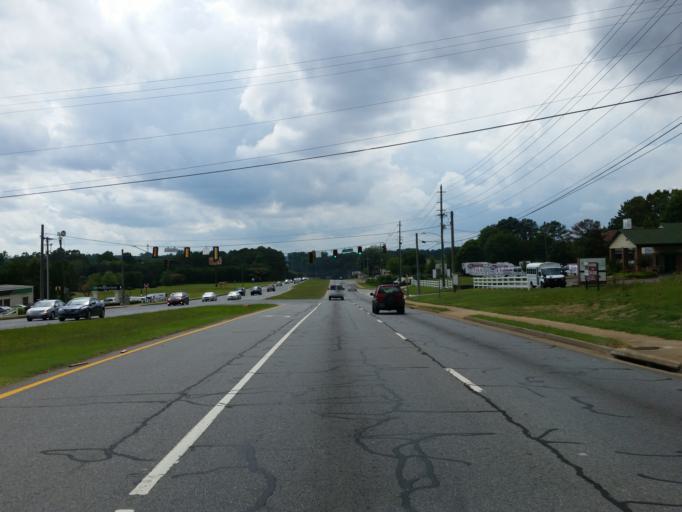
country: US
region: Georgia
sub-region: Cherokee County
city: Woodstock
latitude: 34.0866
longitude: -84.5023
